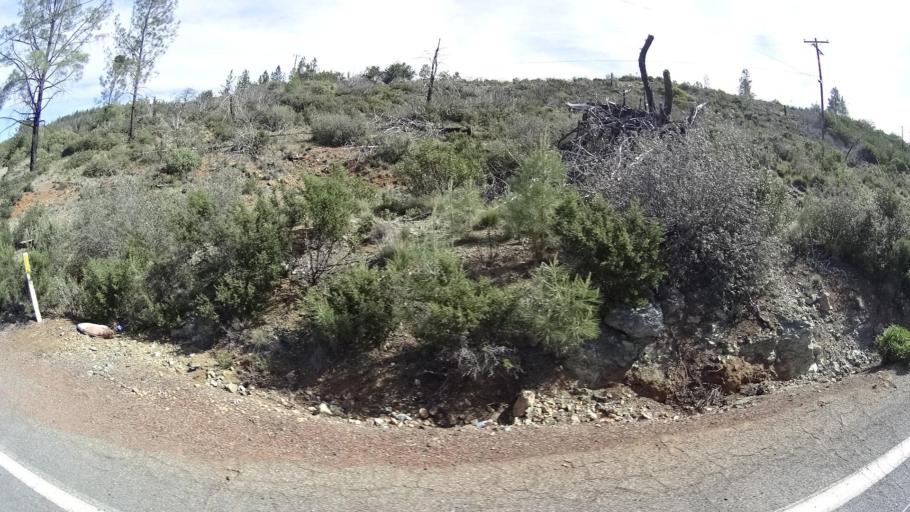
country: US
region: California
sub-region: Lake County
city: Cobb
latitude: 38.8573
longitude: -122.7548
